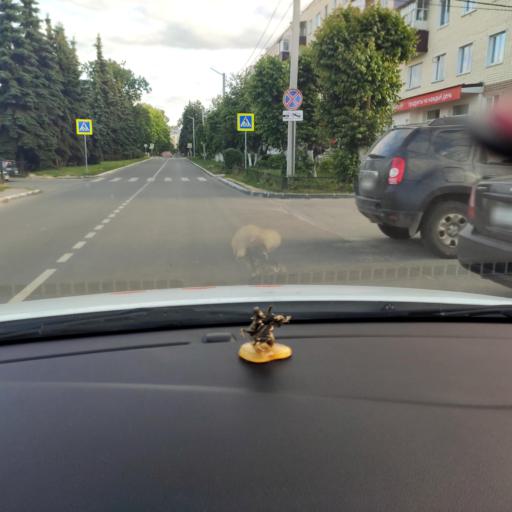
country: RU
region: Tatarstan
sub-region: Zelenodol'skiy Rayon
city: Zelenodolsk
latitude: 55.8500
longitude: 48.4985
